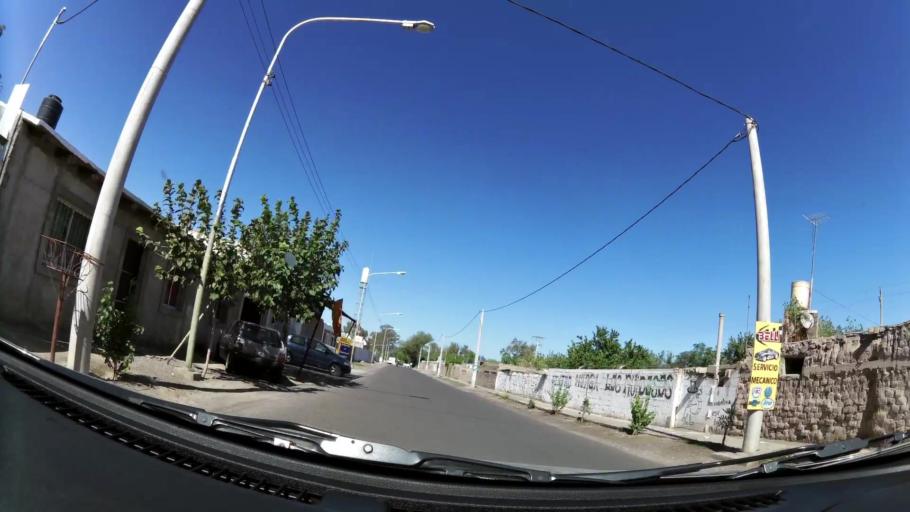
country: AR
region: San Juan
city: San Juan
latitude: -31.5446
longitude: -68.5428
